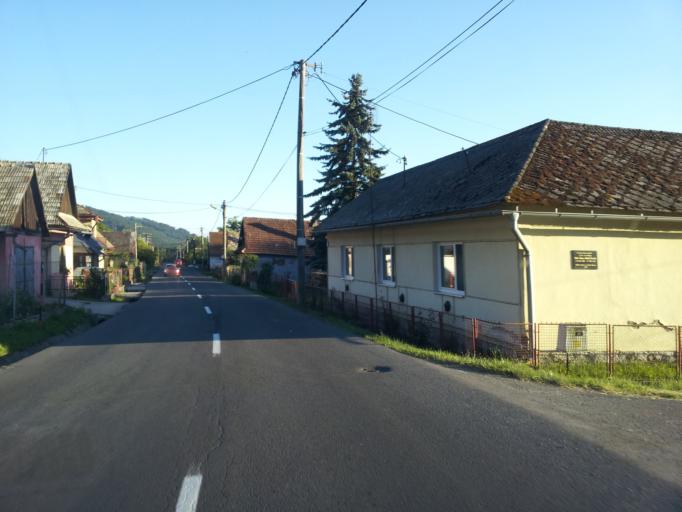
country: SK
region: Banskobystricky
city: Svaety Anton
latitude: 48.4185
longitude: 18.9397
